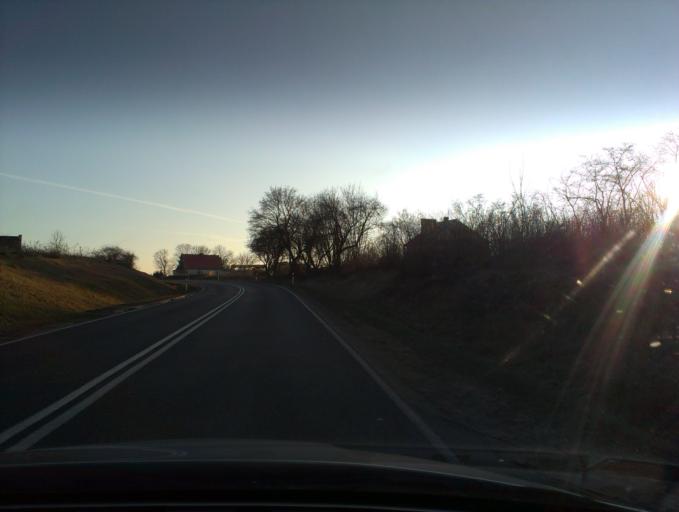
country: PL
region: West Pomeranian Voivodeship
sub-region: Powiat szczecinecki
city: Szczecinek
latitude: 53.6809
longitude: 16.6872
